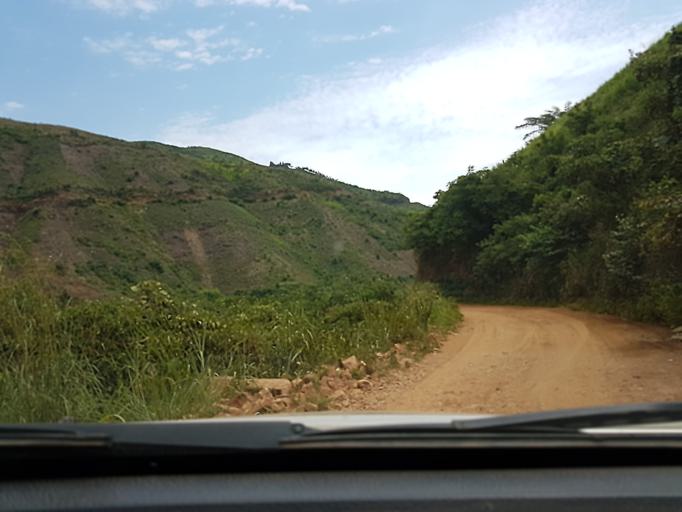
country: RW
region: Western Province
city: Cyangugu
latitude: -2.7080
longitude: 28.9461
